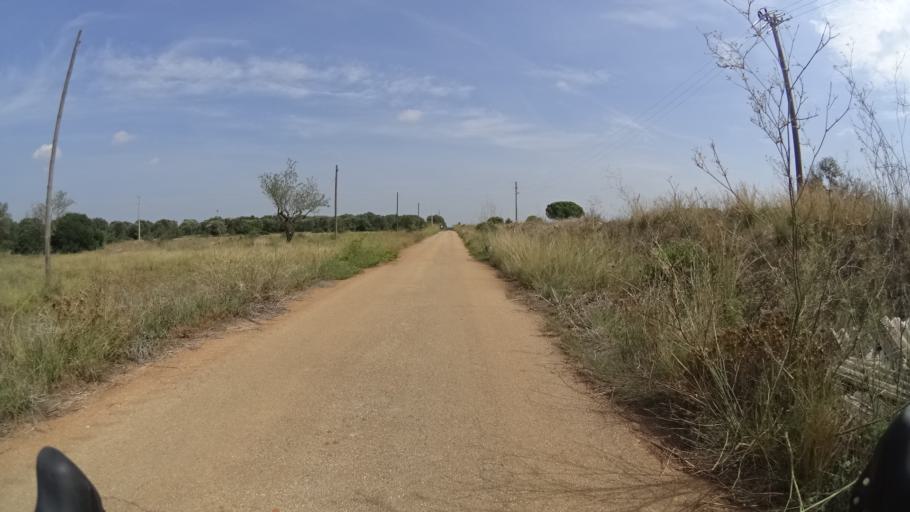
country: IT
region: Apulia
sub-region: Provincia di Brindisi
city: San Pancrazio Salentino
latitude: 40.3456
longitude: 17.8455
